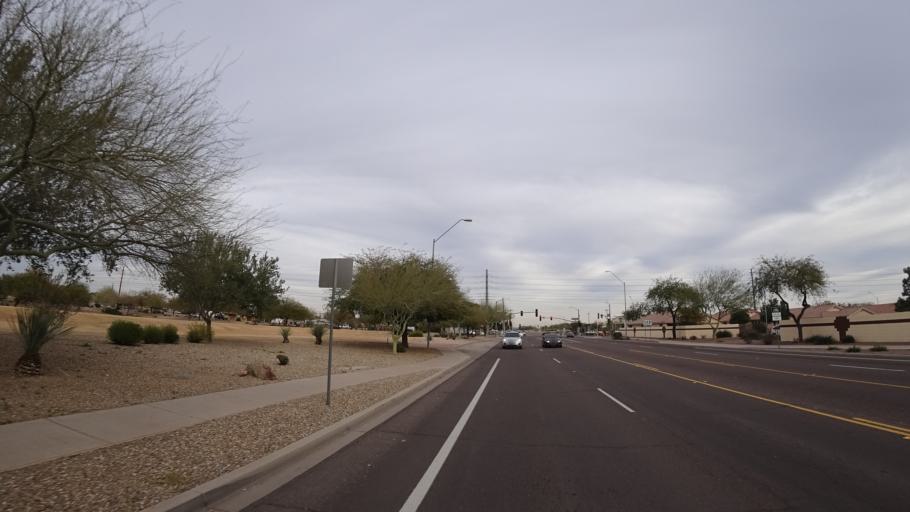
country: US
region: Arizona
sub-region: Maricopa County
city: Surprise
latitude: 33.6236
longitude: -112.3431
